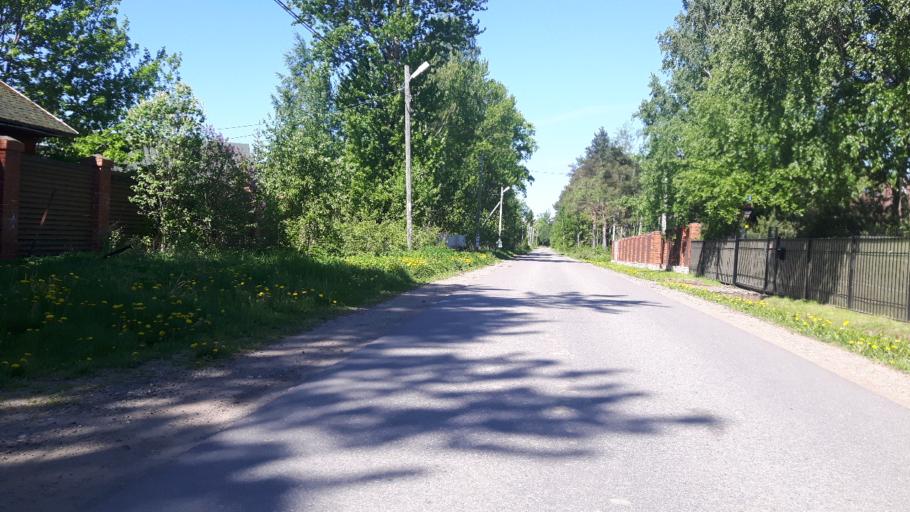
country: RU
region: Leningrad
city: Lebyazh'ye
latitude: 59.9698
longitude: 29.3894
